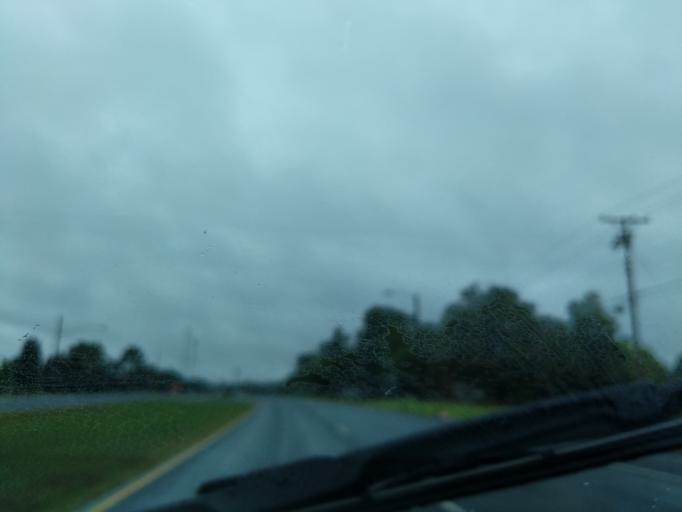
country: US
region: Texas
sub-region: Nacogdoches County
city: Nacogdoches
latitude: 31.6569
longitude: -94.6570
